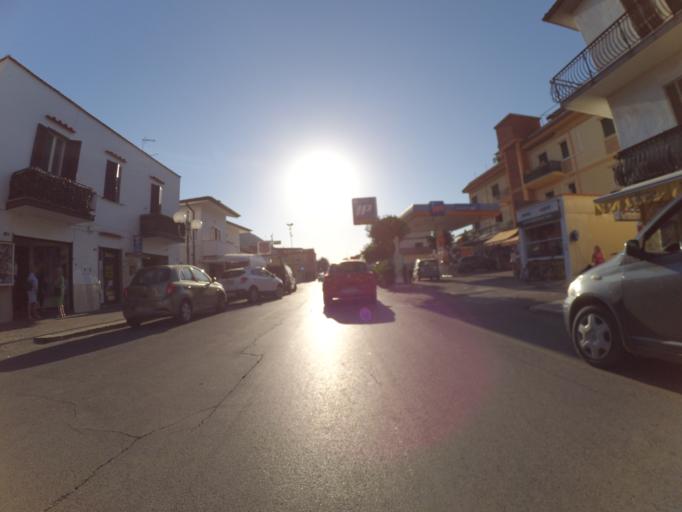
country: IT
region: Latium
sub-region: Provincia di Latina
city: San Felice Circeo
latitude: 41.2429
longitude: 13.0930
